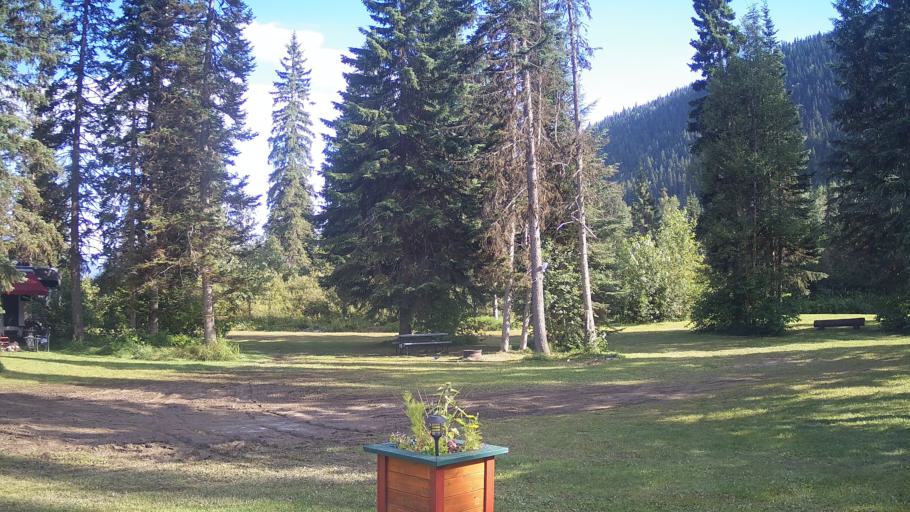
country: CA
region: Alberta
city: Jasper Park Lodge
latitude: 52.6563
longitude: -119.1955
